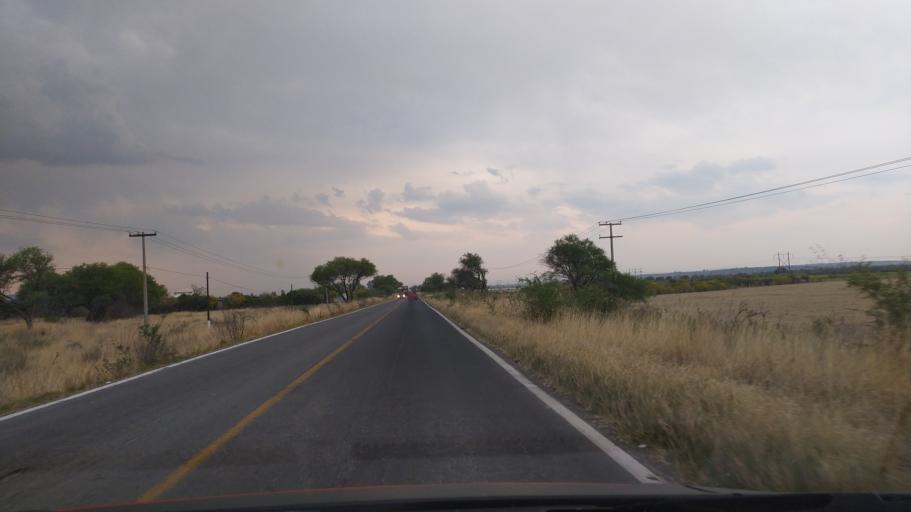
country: MX
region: Guanajuato
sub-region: San Francisco del Rincon
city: San Ignacio de Hidalgo
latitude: 20.8329
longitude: -101.8995
